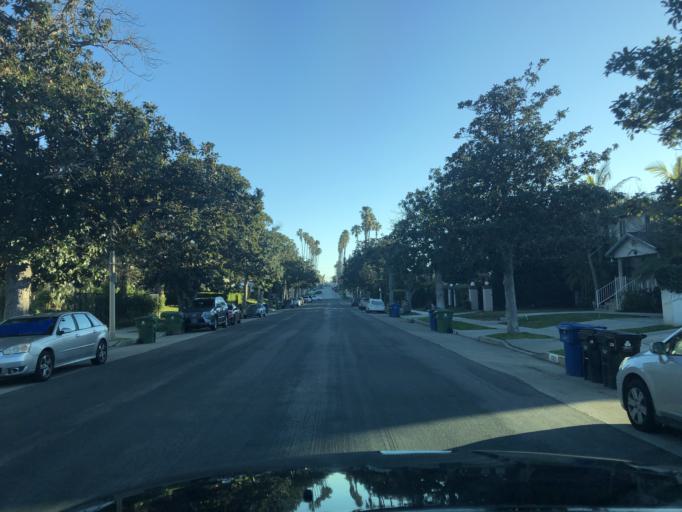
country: US
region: California
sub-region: Los Angeles County
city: Hollywood
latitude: 34.0512
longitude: -118.3146
